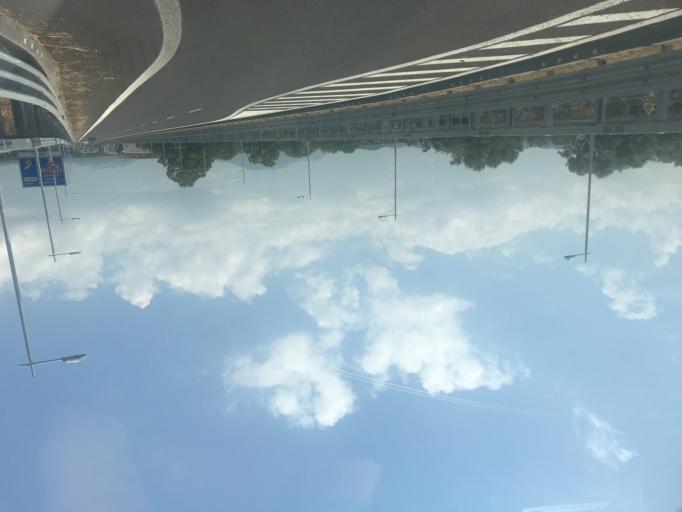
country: IT
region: Sardinia
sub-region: Provincia di Olbia-Tempio
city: Olbia
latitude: 40.9024
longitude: 9.5072
